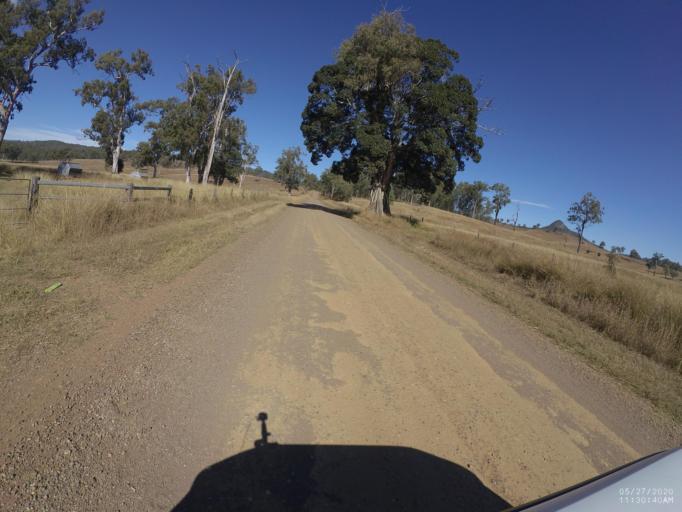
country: AU
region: Queensland
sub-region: Ipswich
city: Redbank Plains
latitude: -27.7394
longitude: 152.8314
